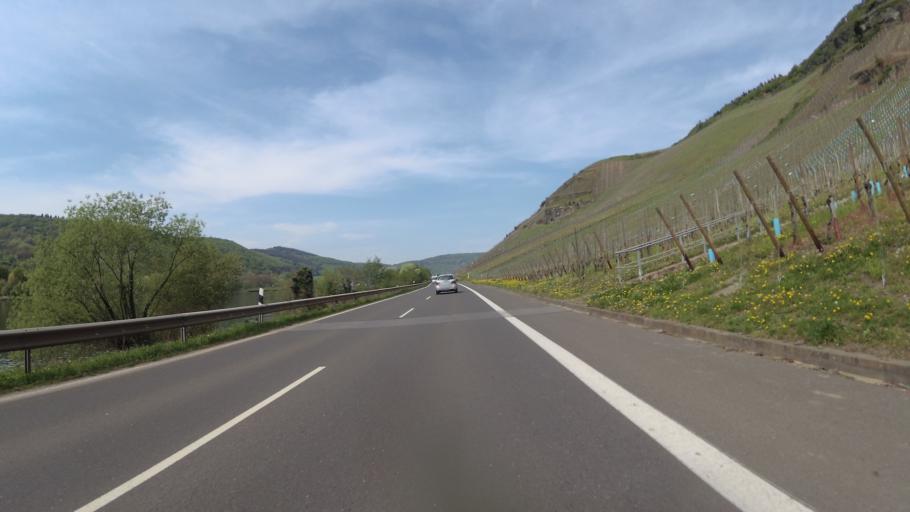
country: DE
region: Rheinland-Pfalz
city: Losnich
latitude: 49.9471
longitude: 7.0370
